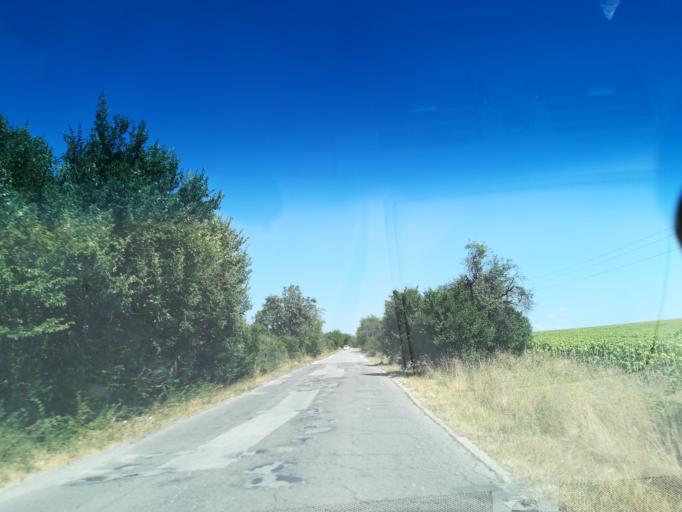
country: BG
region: Plovdiv
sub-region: Obshtina Sadovo
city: Sadovo
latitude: 42.0238
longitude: 25.0031
